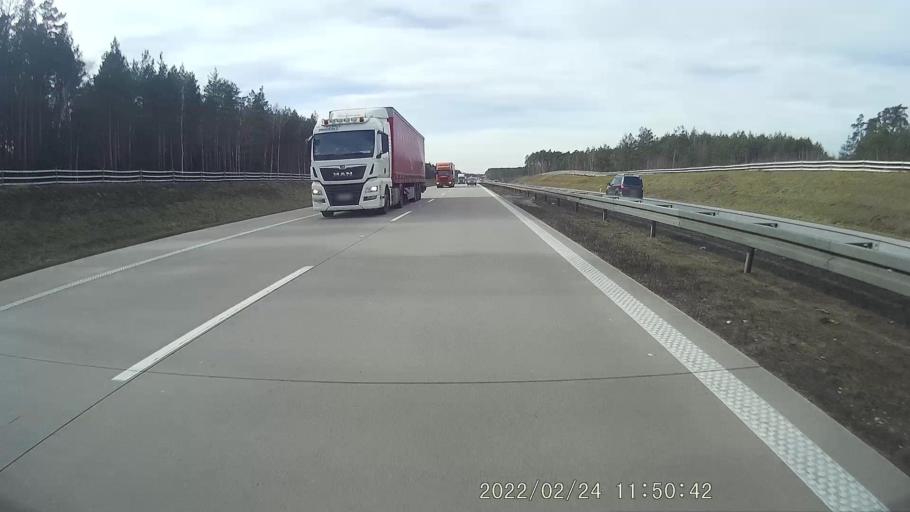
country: PL
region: Lower Silesian Voivodeship
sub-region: Powiat polkowicki
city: Radwanice
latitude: 51.6037
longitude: 15.9646
